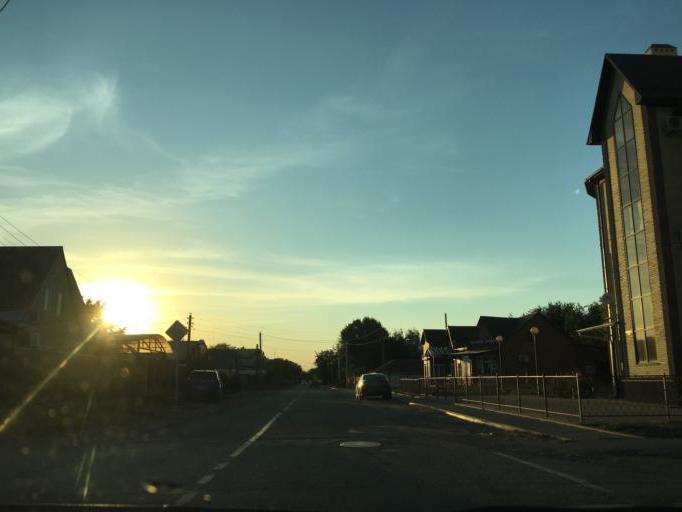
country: RU
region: Krasnodarskiy
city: Kushchevskaya
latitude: 46.5681
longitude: 39.6291
